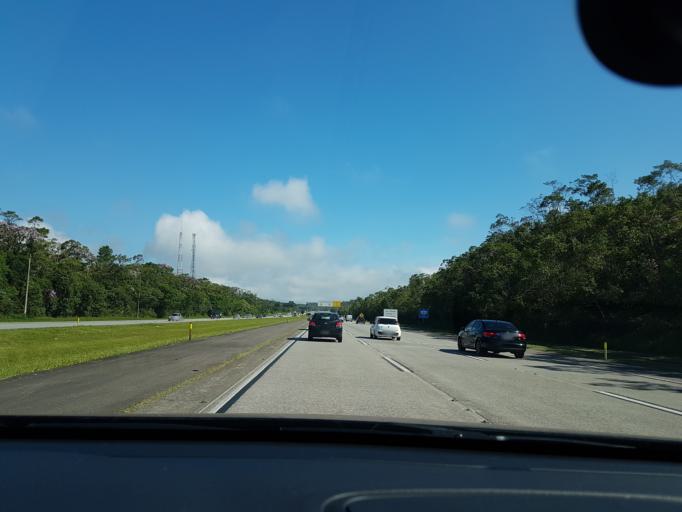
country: BR
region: Sao Paulo
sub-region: Cubatao
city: Cubatao
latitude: -23.9066
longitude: -46.5596
